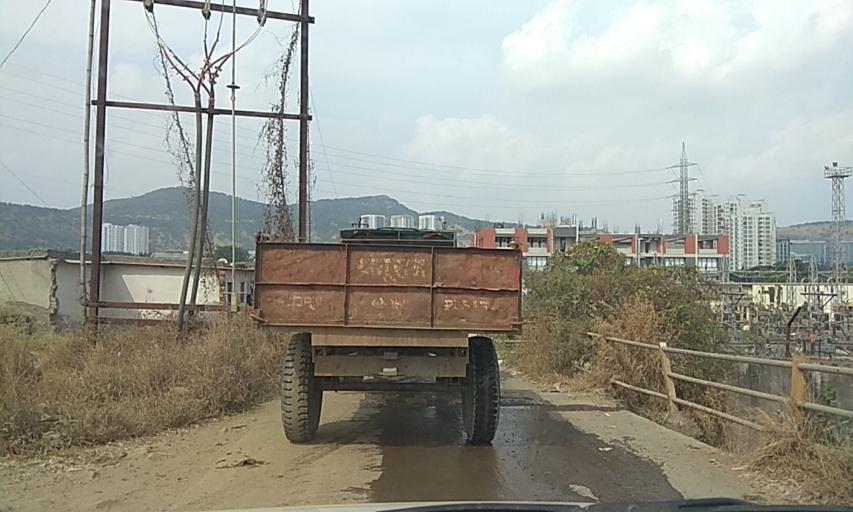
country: IN
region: Maharashtra
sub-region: Pune Division
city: Pimpri
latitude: 18.5875
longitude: 73.7057
